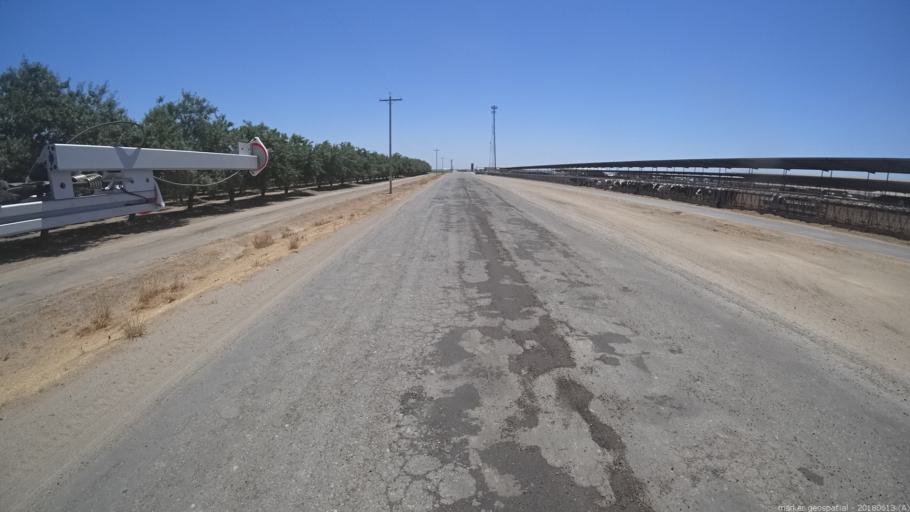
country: US
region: California
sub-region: Madera County
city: Fairmead
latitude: 36.9914
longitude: -120.2741
